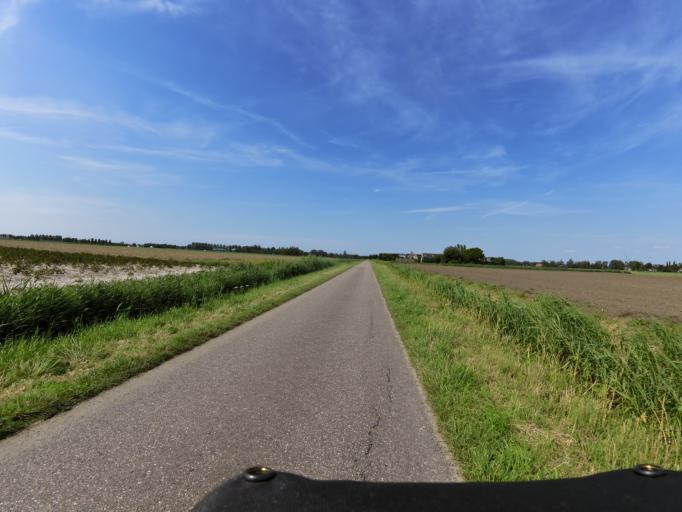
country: NL
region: South Holland
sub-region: Gemeente Goeree-Overflakkee
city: Middelharnis
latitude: 51.7457
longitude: 4.1409
